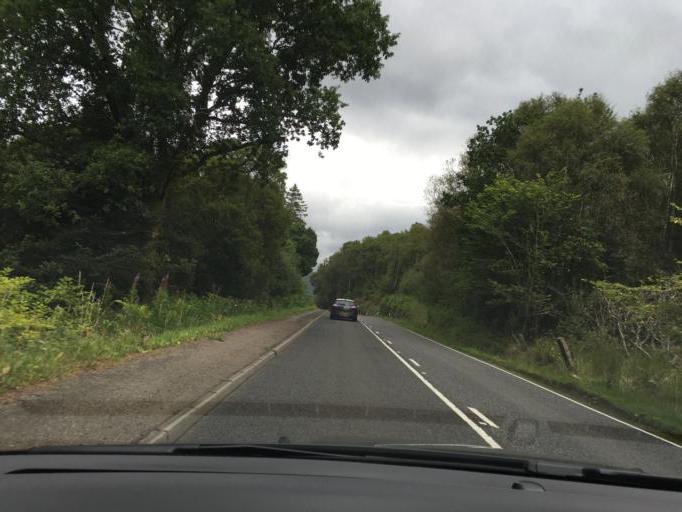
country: GB
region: Scotland
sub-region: Highland
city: Fort William
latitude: 56.7801
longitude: -5.1632
